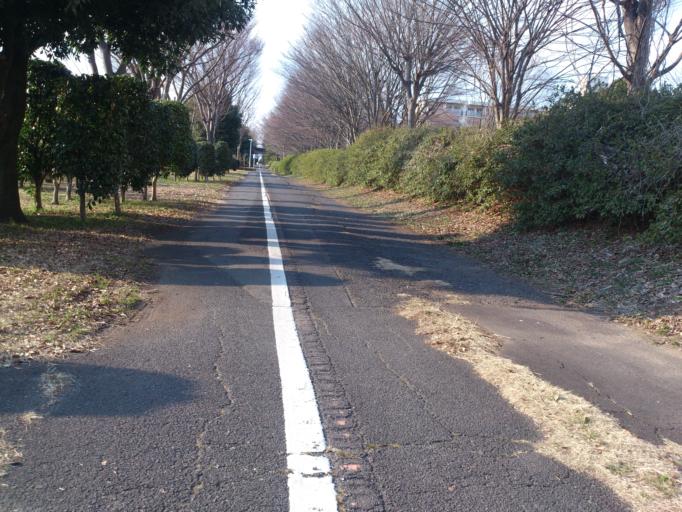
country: JP
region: Ibaraki
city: Naka
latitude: 36.0828
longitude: 140.1066
